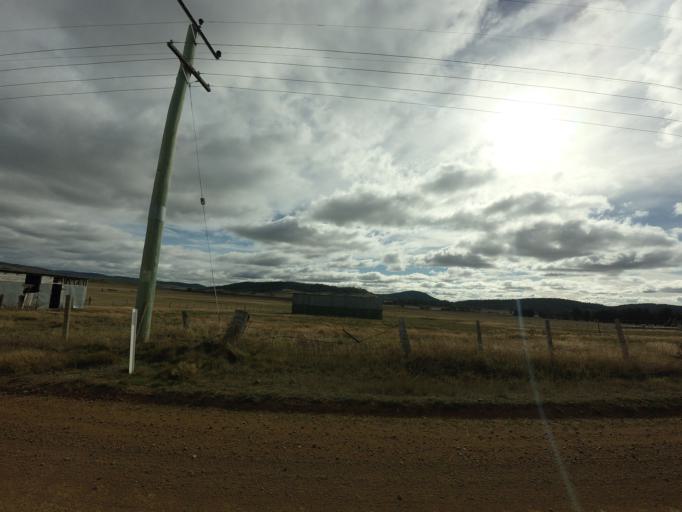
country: AU
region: Tasmania
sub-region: Brighton
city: Bridgewater
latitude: -42.4164
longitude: 147.3950
